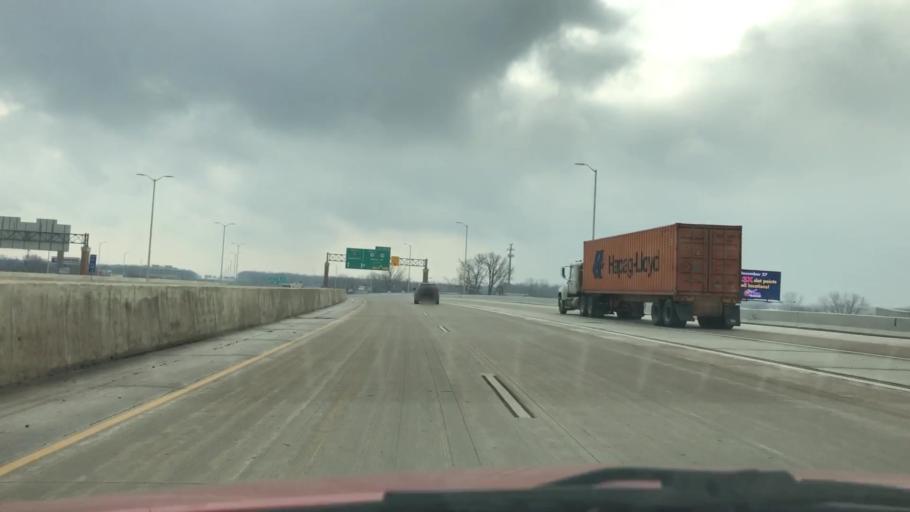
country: US
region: Wisconsin
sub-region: Brown County
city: Howard
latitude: 44.5344
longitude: -88.0810
